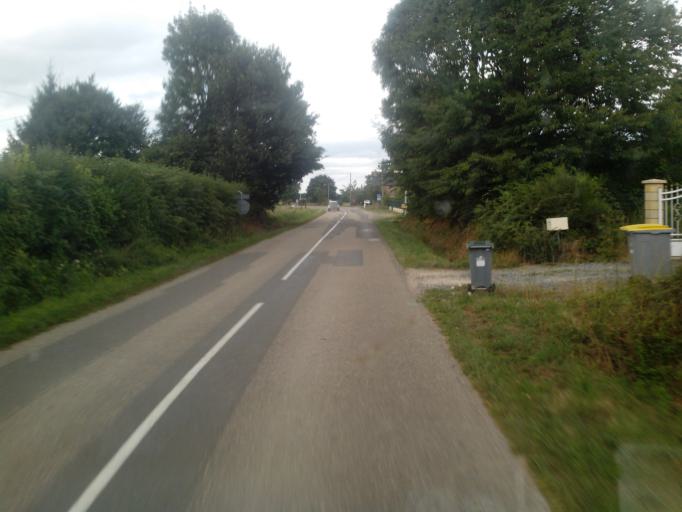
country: FR
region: Brittany
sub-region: Departement d'Ille-et-Vilaine
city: Maxent
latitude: 47.9655
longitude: -2.0162
